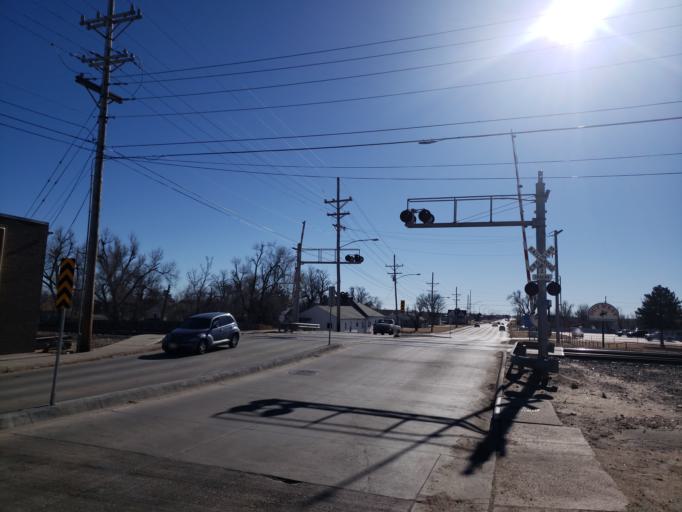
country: US
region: Kansas
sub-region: Ford County
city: Dodge City
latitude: 37.7533
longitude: -100.0330
